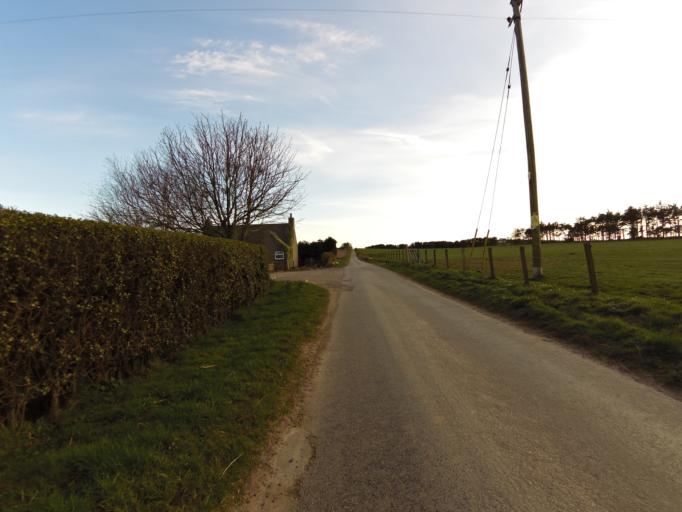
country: GB
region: Scotland
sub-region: Aberdeenshire
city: Stonehaven
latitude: 56.9428
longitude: -2.2207
